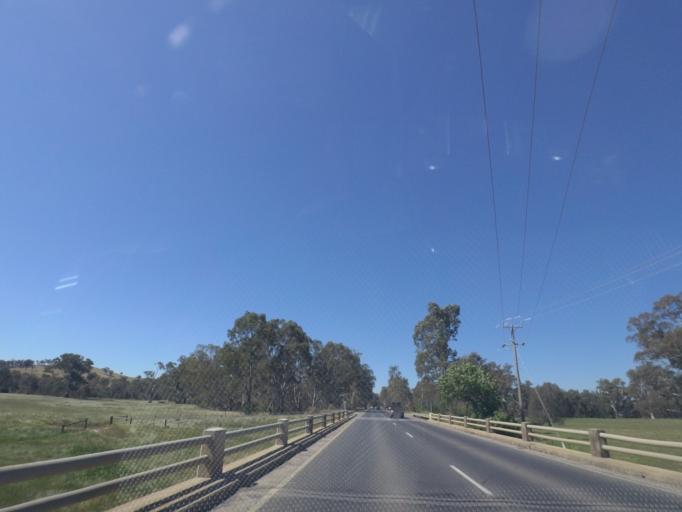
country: AU
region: Victoria
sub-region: Murrindindi
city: Kinglake West
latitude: -37.0264
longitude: 145.1098
